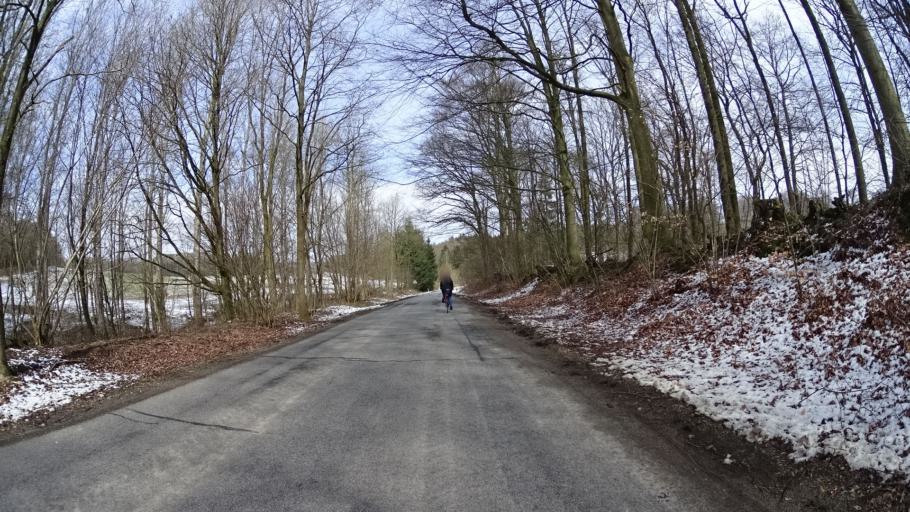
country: DE
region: Schleswig-Holstein
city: Stolpe
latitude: 54.1415
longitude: 10.2305
